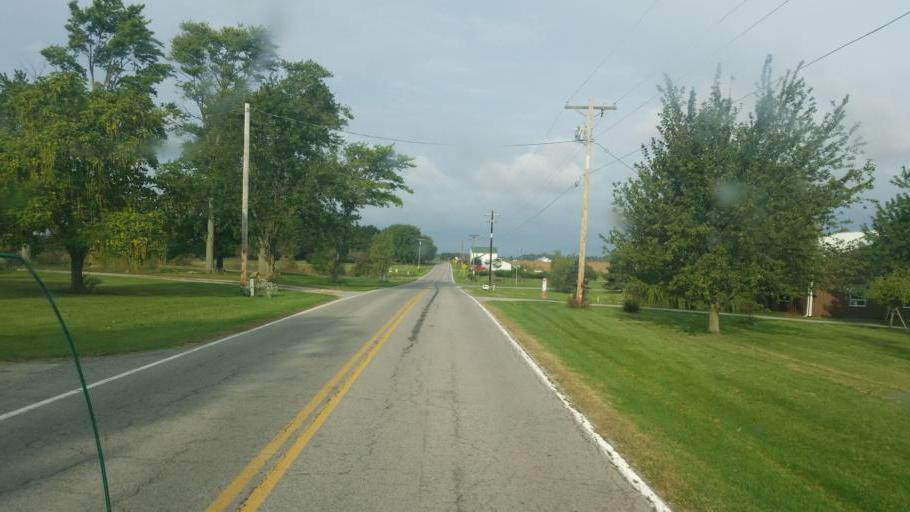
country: US
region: Ohio
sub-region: Wyandot County
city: Carey
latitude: 41.0348
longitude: -83.4638
